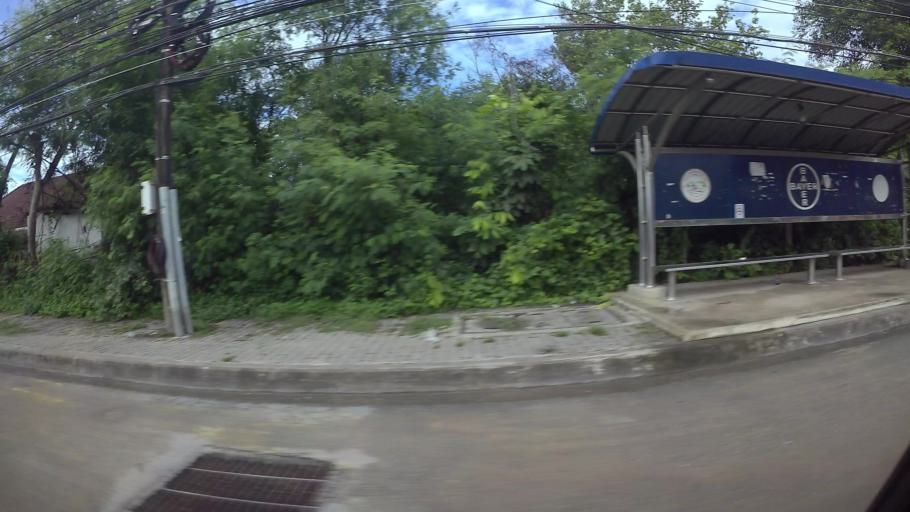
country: TH
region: Rayong
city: Rayong
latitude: 12.7043
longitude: 101.1834
